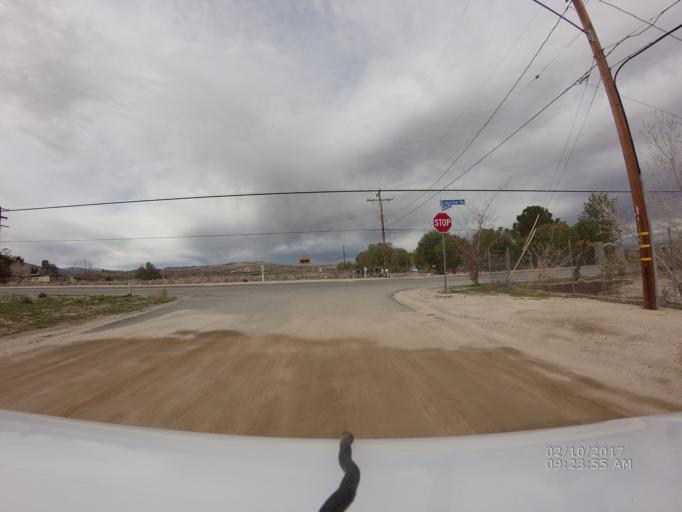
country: US
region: California
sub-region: Los Angeles County
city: Littlerock
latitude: 34.4955
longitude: -117.8964
